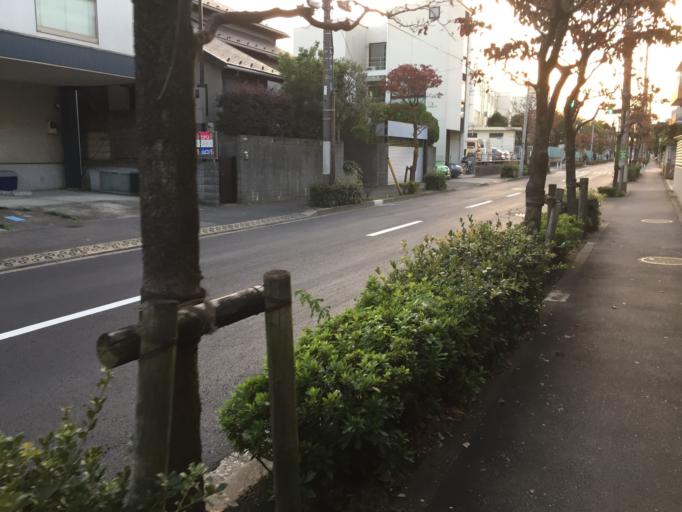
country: JP
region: Tokyo
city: Tokyo
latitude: 35.6399
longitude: 139.6538
